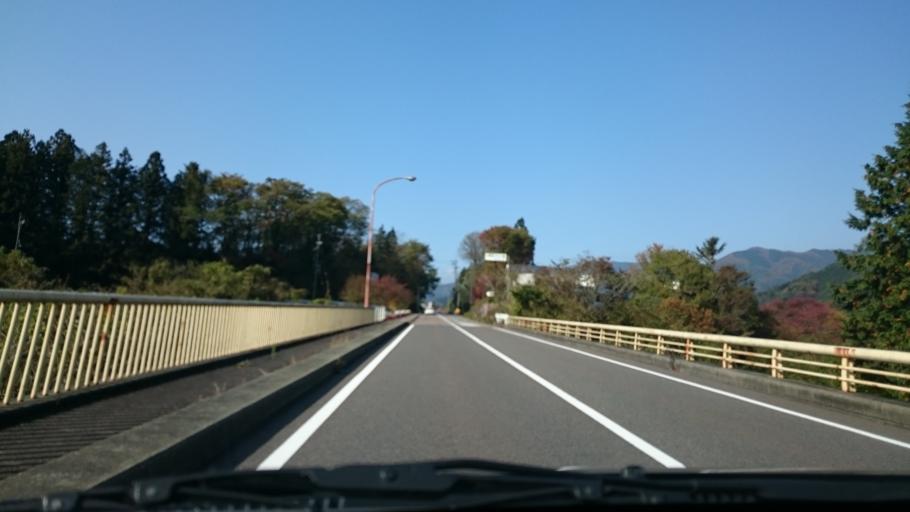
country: JP
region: Gifu
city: Nakatsugawa
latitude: 35.7361
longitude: 137.3436
